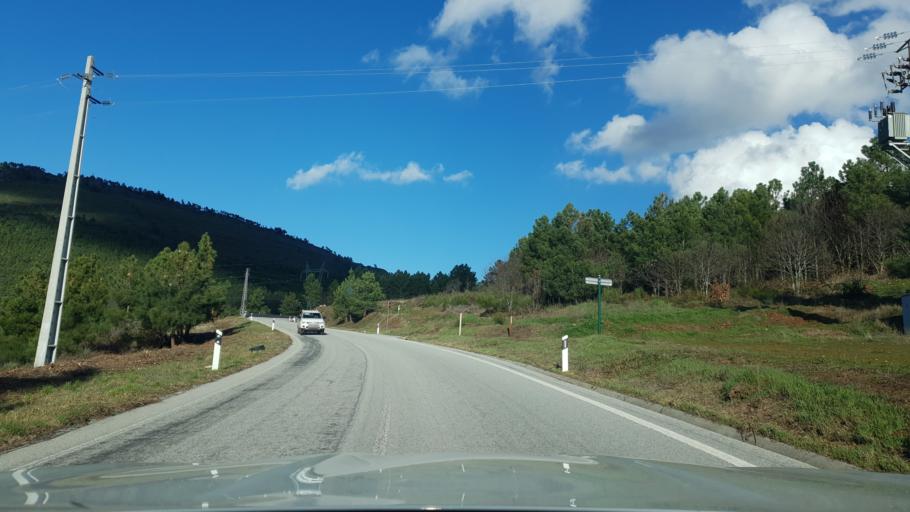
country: PT
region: Braganca
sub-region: Torre de Moncorvo
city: Torre de Moncorvo
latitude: 41.1868
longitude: -6.9603
